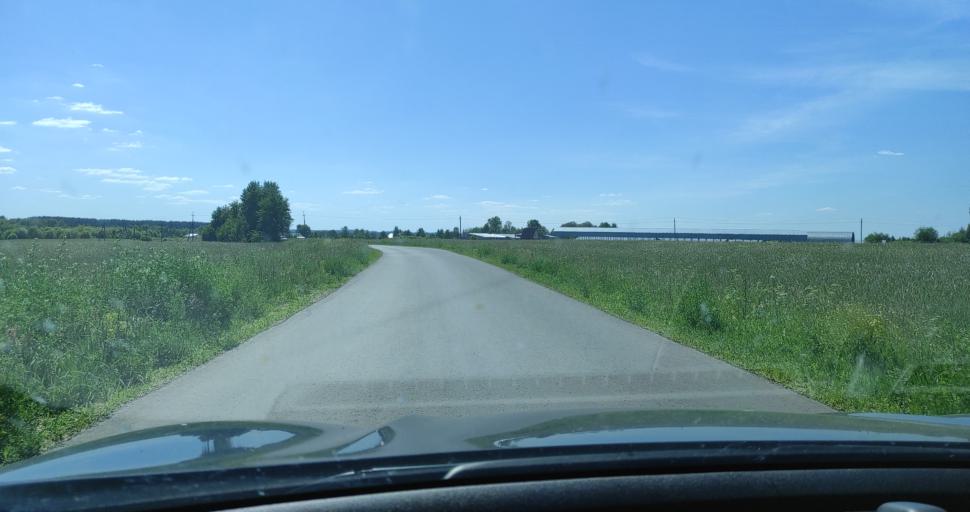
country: RU
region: Rjazan
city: Murmino
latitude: 54.5701
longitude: 40.0985
